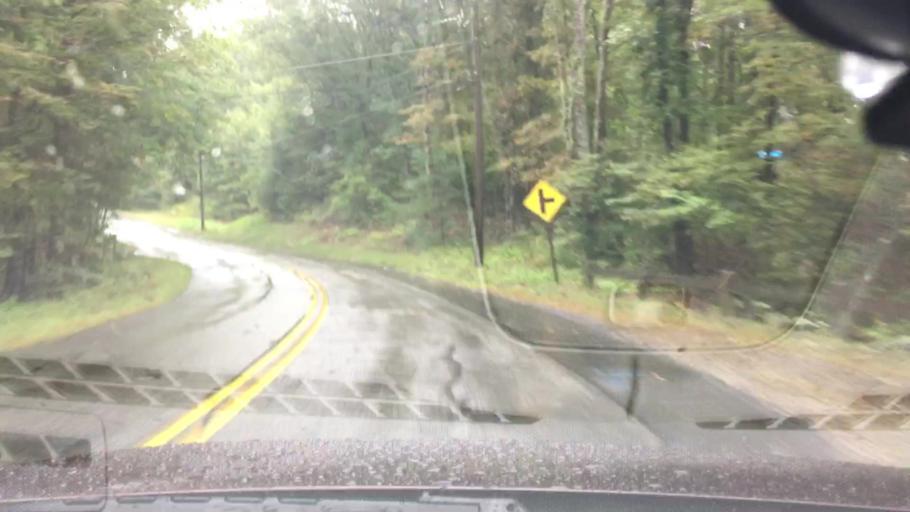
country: US
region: Connecticut
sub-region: Tolland County
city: Storrs
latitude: 41.8127
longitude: -72.2861
